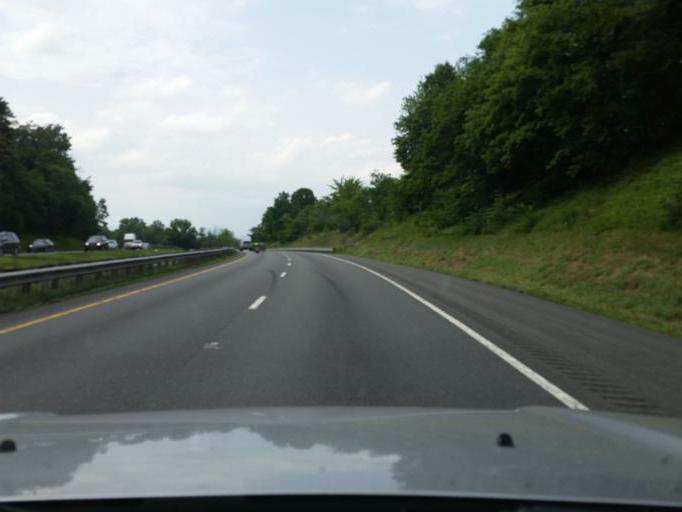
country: US
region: Maryland
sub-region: Frederick County
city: Urbana
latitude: 39.2938
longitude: -77.3326
